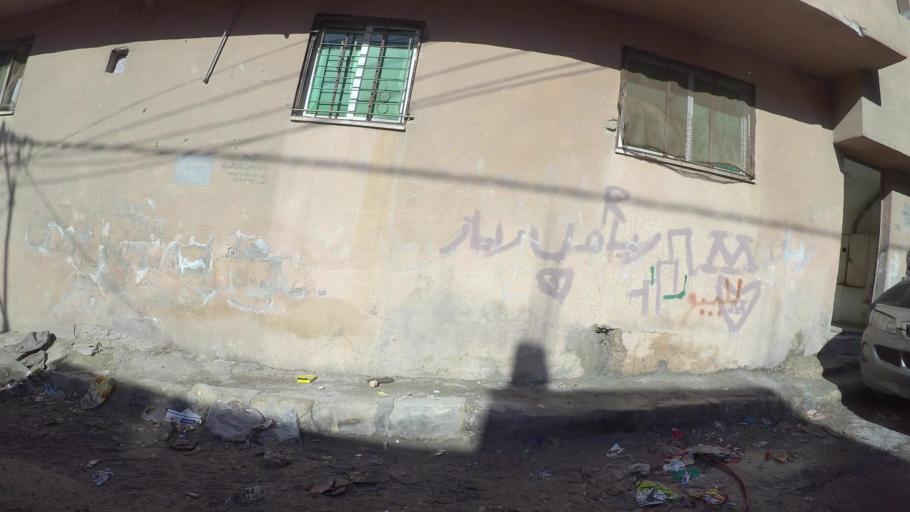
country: JO
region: Amman
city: Al Jubayhah
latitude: 32.0761
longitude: 35.8516
